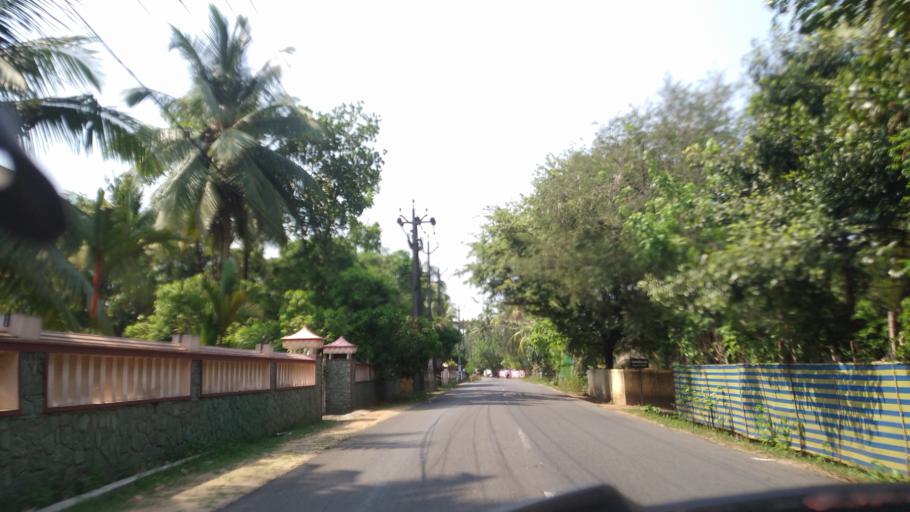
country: IN
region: Kerala
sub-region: Thrissur District
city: Thanniyam
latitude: 10.3385
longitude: 76.1181
